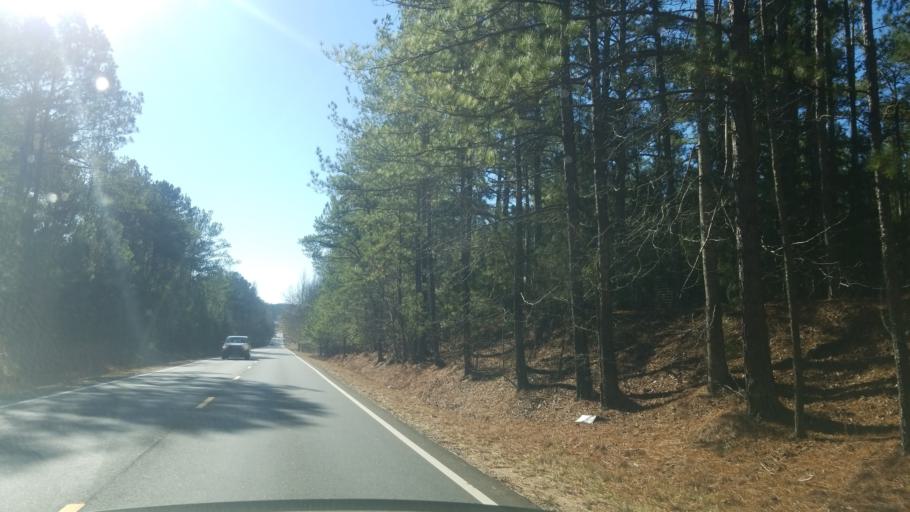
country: US
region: Alabama
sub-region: Chambers County
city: Valley
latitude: 32.8015
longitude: -85.1029
